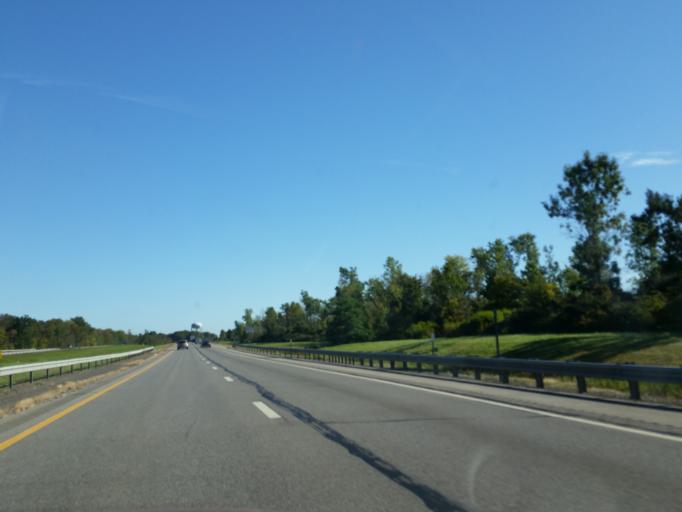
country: US
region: New York
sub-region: Erie County
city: Hamburg
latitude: 42.7518
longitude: -78.8321
